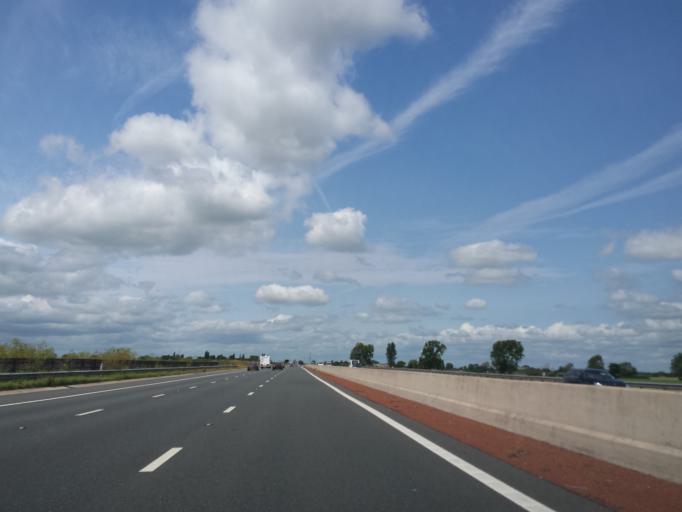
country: GB
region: England
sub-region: North Yorkshire
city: Ripon
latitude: 54.2090
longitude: -1.4765
